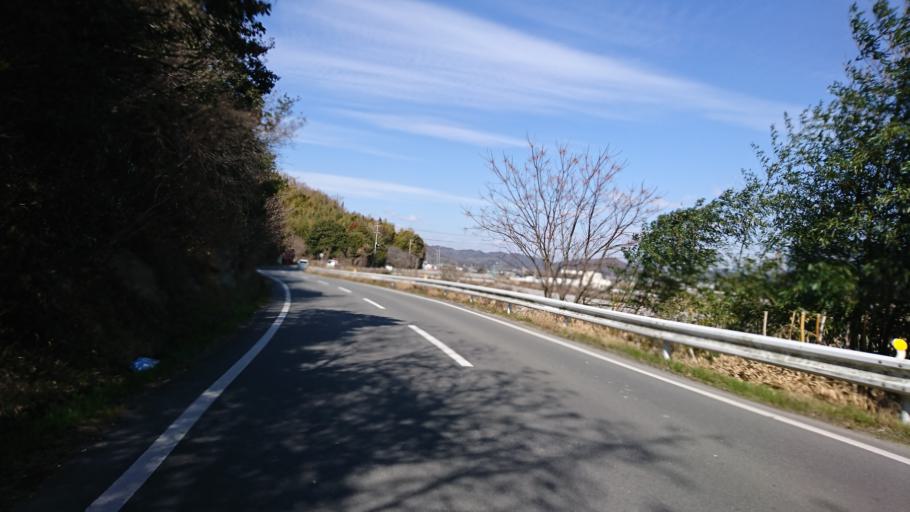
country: JP
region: Hyogo
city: Kakogawacho-honmachi
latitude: 34.8007
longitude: 134.8112
